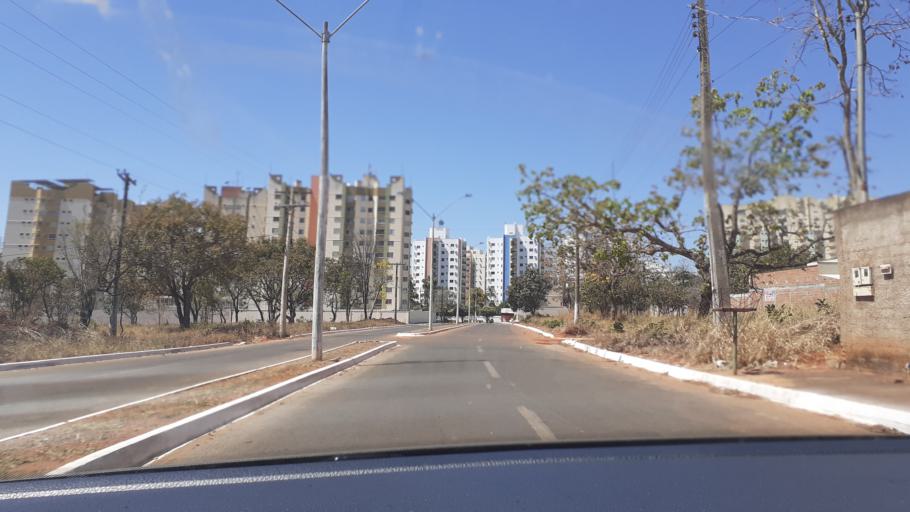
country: BR
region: Goias
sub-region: Caldas Novas
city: Caldas Novas
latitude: -17.7383
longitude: -48.6374
